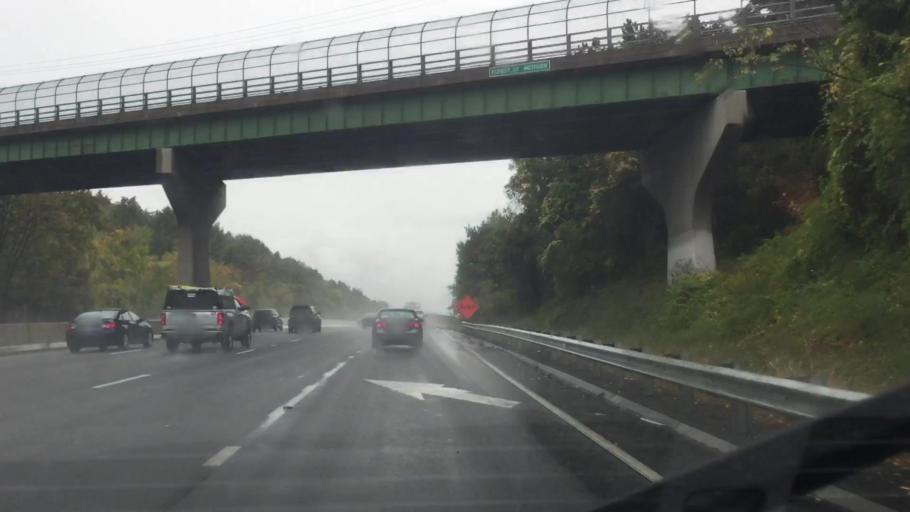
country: US
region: Massachusetts
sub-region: Essex County
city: Methuen
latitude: 42.7093
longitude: -71.2108
